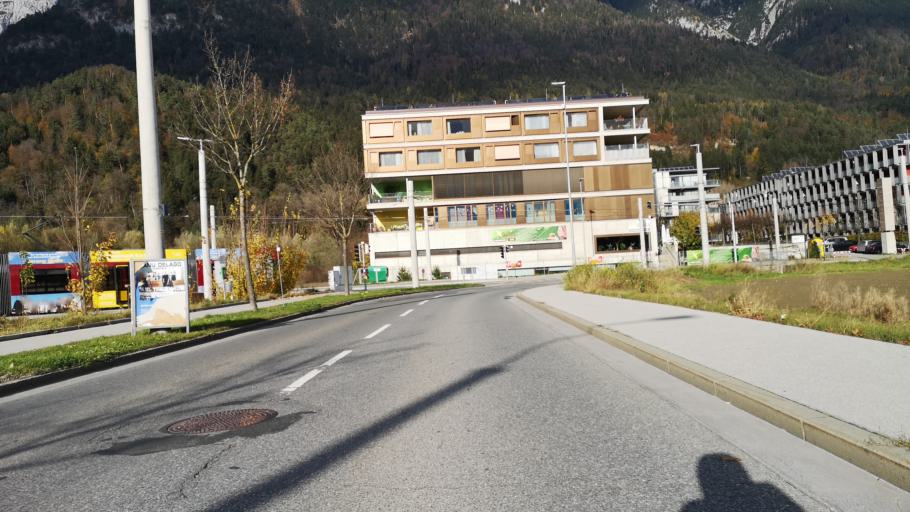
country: AT
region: Tyrol
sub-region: Politischer Bezirk Innsbruck Land
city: Vols
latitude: 47.2643
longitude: 11.3394
